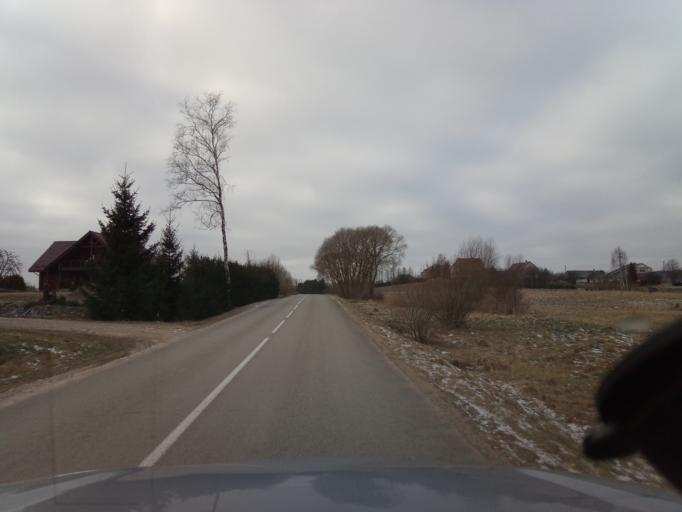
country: LT
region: Alytaus apskritis
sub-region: Alytaus rajonas
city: Daugai
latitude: 54.3550
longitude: 24.3322
